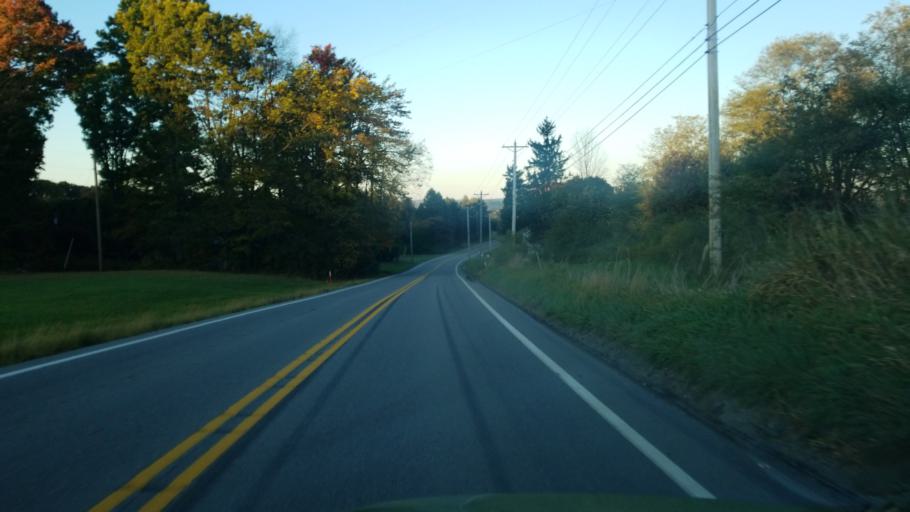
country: US
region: Pennsylvania
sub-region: Jefferson County
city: Reynoldsville
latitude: 41.0613
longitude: -78.9291
